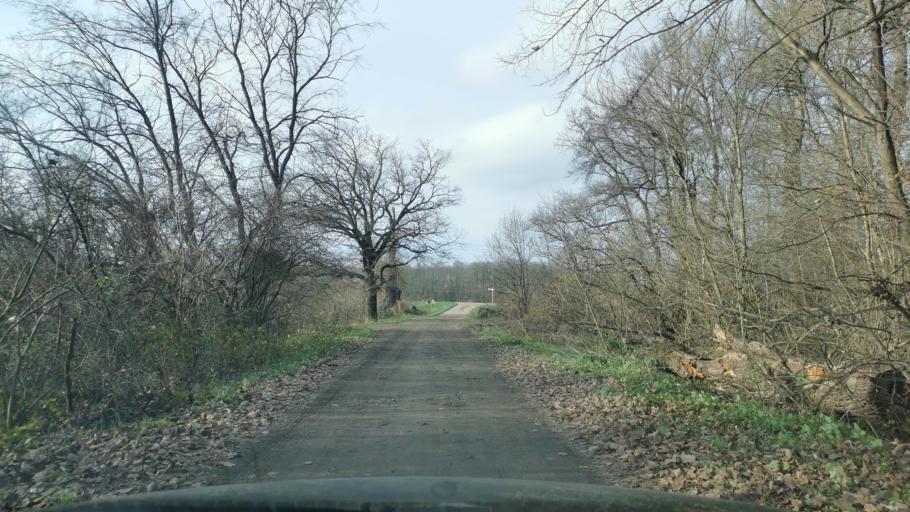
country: CZ
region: South Moravian
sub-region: Okres Hodonin
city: Mikulcice
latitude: 48.7844
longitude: 17.0907
